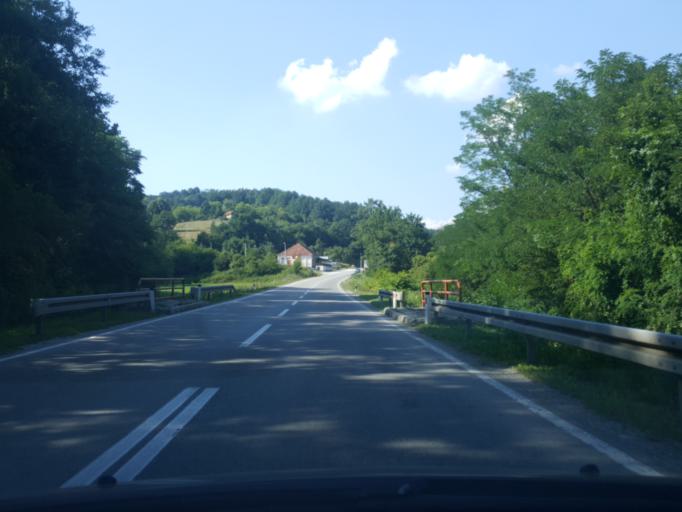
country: RS
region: Central Serbia
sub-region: Moravicki Okrug
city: Gornji Milanovac
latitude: 44.0983
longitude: 20.4813
